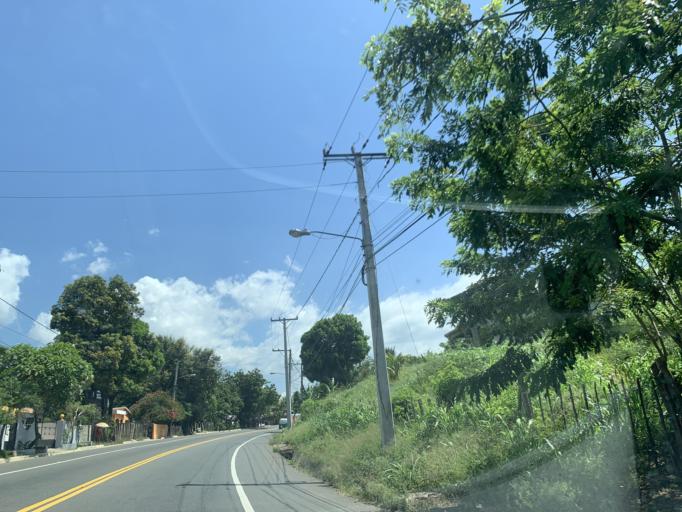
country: DO
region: Puerto Plata
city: Imbert
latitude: 19.7278
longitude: -70.8287
